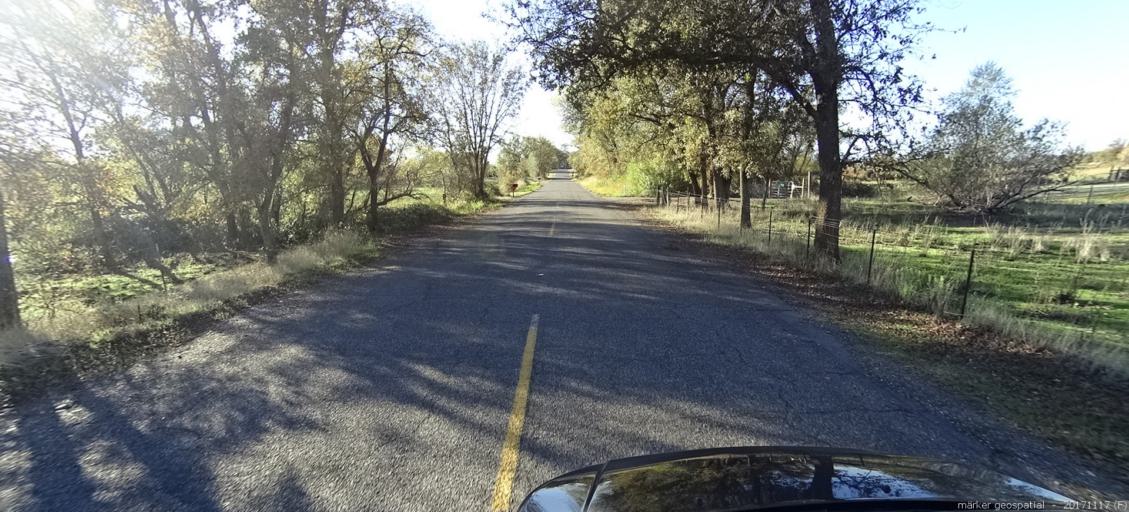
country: US
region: California
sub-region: Shasta County
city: Cottonwood
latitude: 40.3919
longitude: -122.2081
